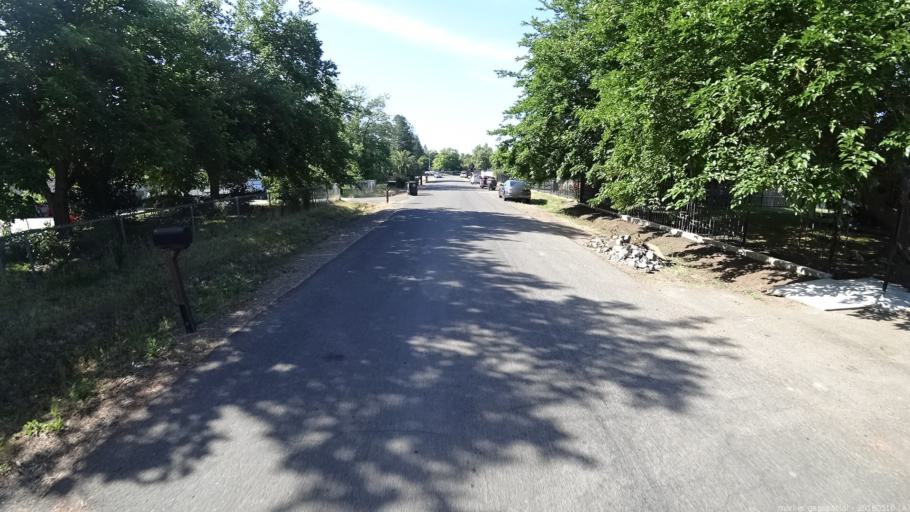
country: US
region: California
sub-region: Sacramento County
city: Rio Linda
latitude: 38.6576
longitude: -121.4801
